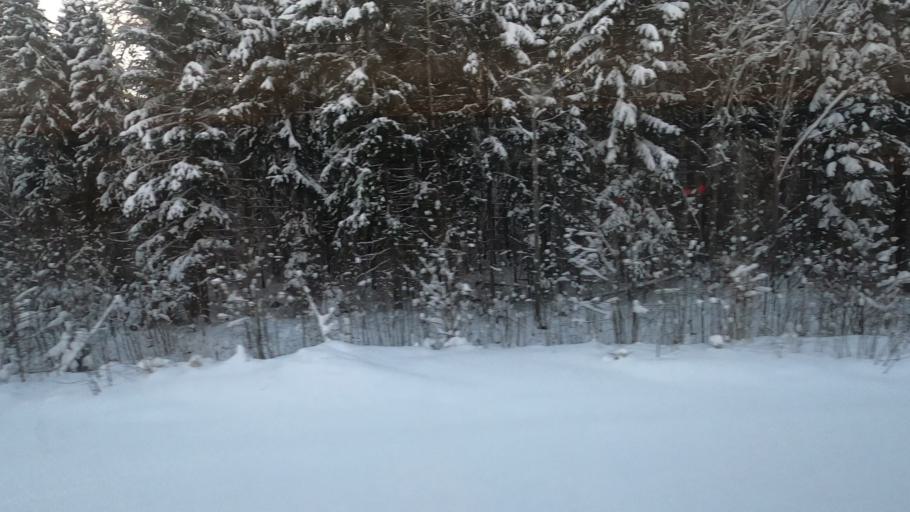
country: RU
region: Moskovskaya
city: Novo-Nikol'skoye
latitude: 56.6177
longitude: 37.5660
